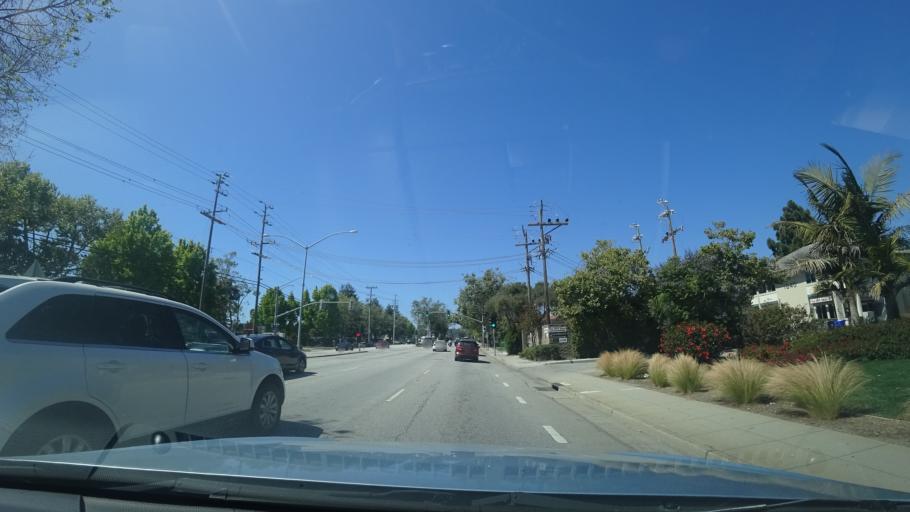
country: US
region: California
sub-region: Santa Cruz County
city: Capitola
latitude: 36.9759
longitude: -121.9646
